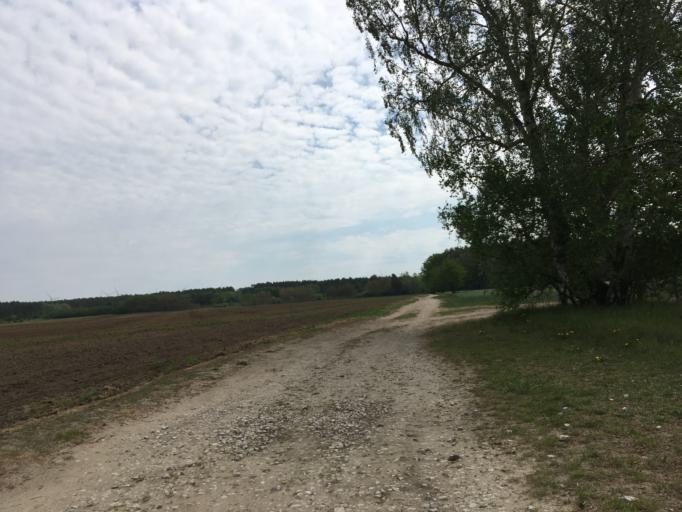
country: DE
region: Brandenburg
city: Rudnitz
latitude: 52.7141
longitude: 13.6224
